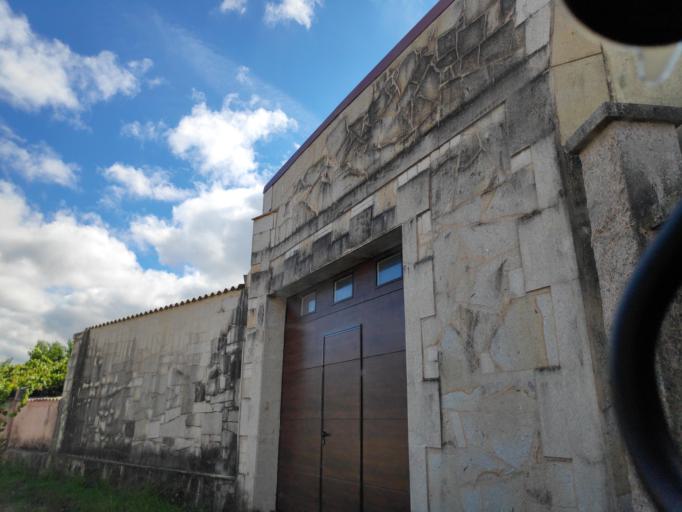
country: ES
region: Galicia
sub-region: Provincia da Coruna
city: Rianxo
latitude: 42.6754
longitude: -8.8209
